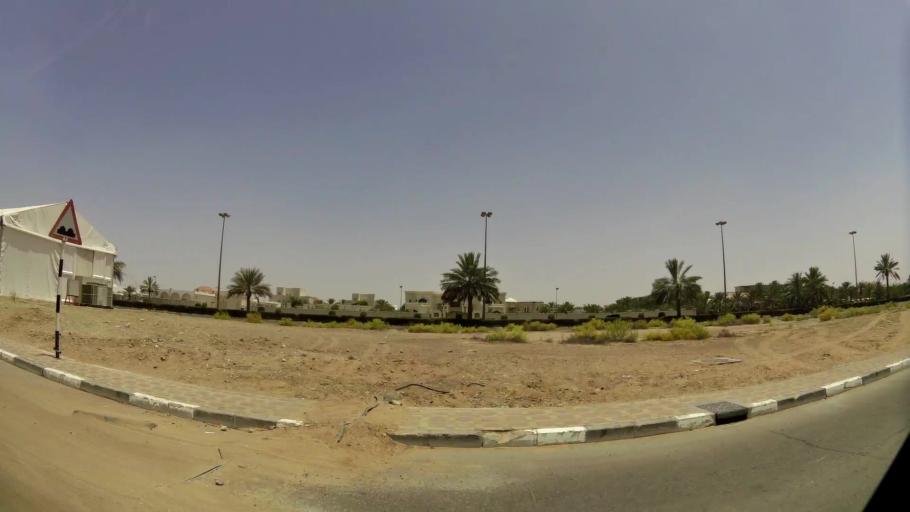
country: OM
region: Al Buraimi
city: Al Buraymi
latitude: 24.2596
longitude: 55.7173
